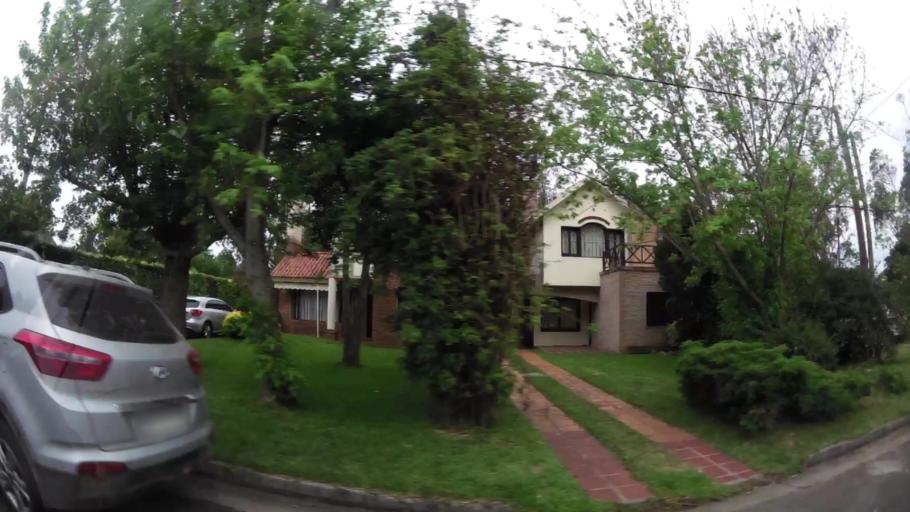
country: UY
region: Maldonado
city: Maldonado
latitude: -34.9140
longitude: -54.9726
